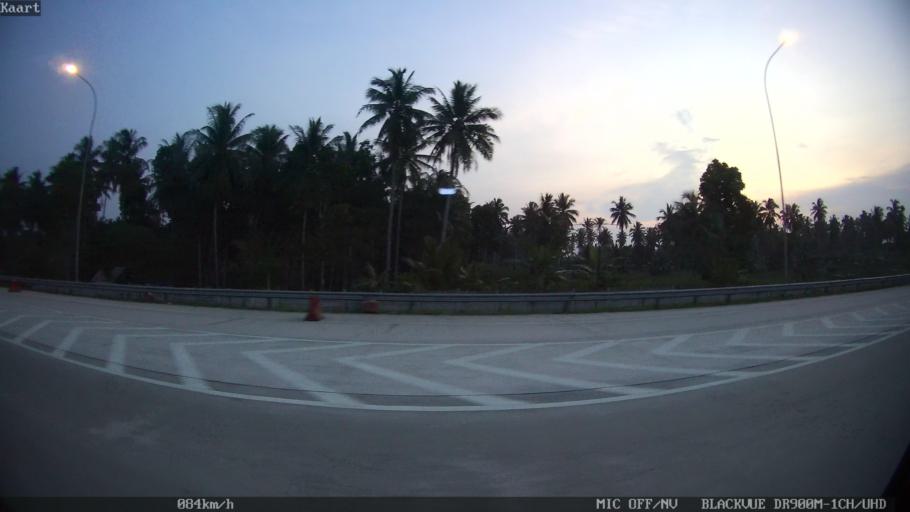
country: ID
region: Lampung
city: Kalianda
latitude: -5.6506
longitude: 105.5824
